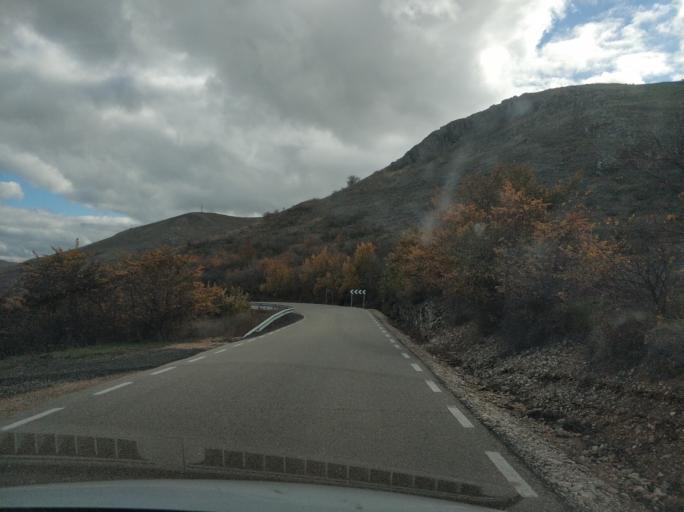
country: ES
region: Castille and Leon
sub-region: Provincia de Soria
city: Medinaceli
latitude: 41.1643
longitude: -2.4326
